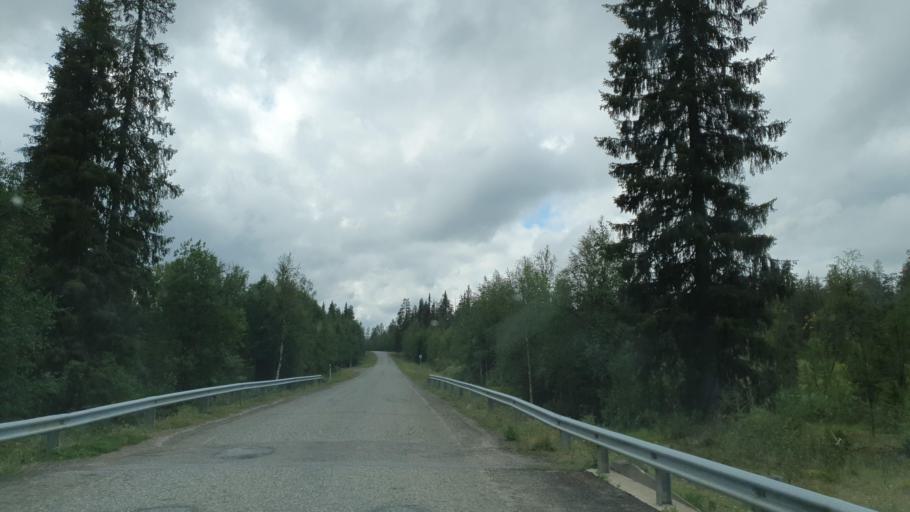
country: FI
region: Lapland
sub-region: Tunturi-Lappi
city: Muonio
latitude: 67.7180
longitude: 24.2215
